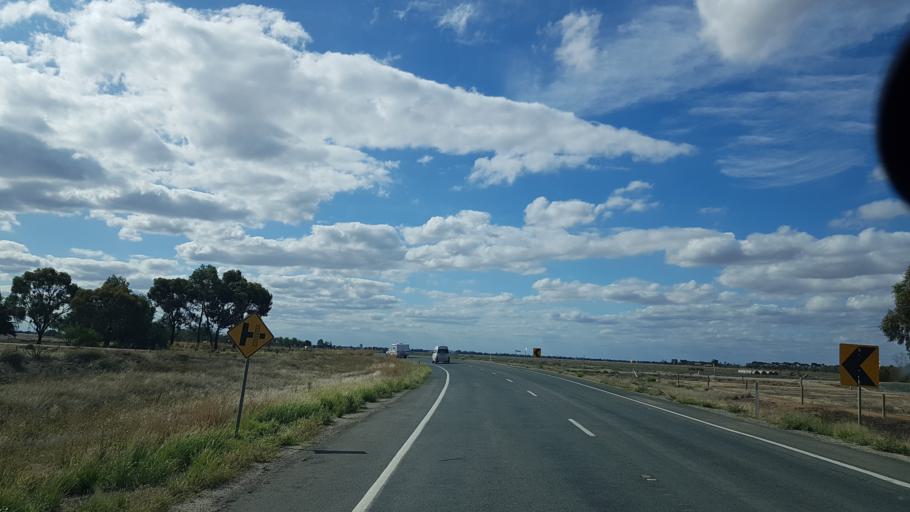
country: AU
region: Victoria
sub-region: Swan Hill
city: Swan Hill
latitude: -35.8013
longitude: 143.9554
